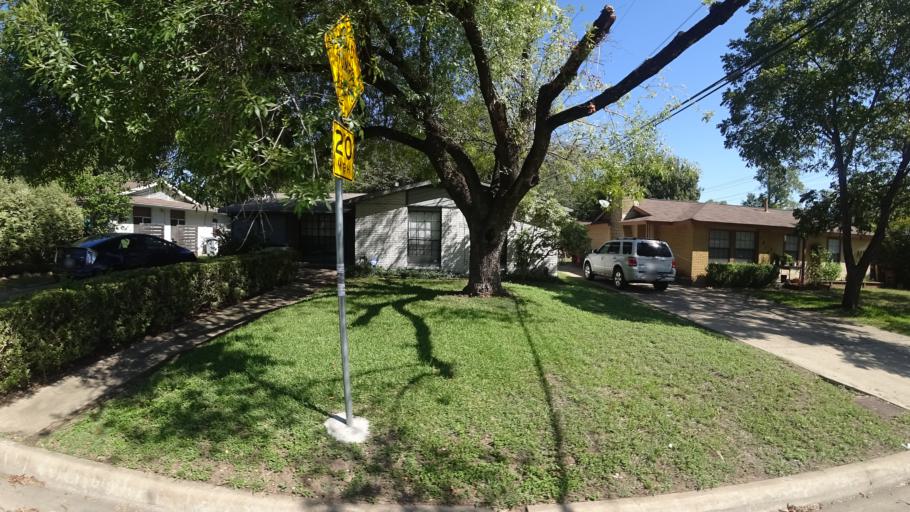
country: US
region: Texas
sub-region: Travis County
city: Austin
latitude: 30.3066
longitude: -97.6978
